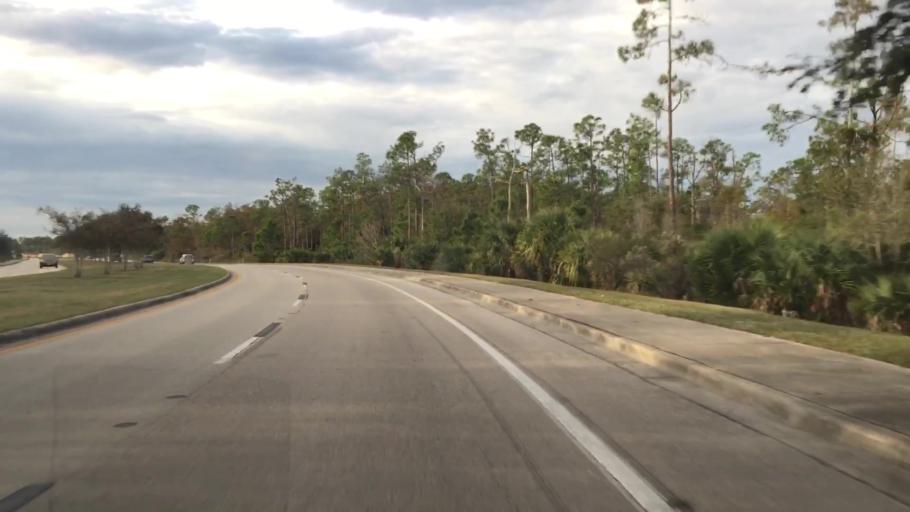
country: US
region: Florida
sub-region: Lee County
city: Gateway
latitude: 26.6022
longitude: -81.7860
